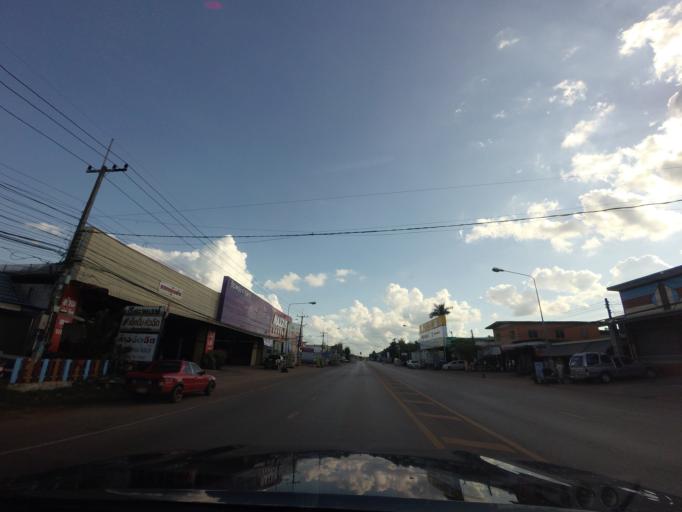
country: TH
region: Changwat Udon Thani
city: Ban Dung
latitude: 17.6864
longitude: 103.2563
